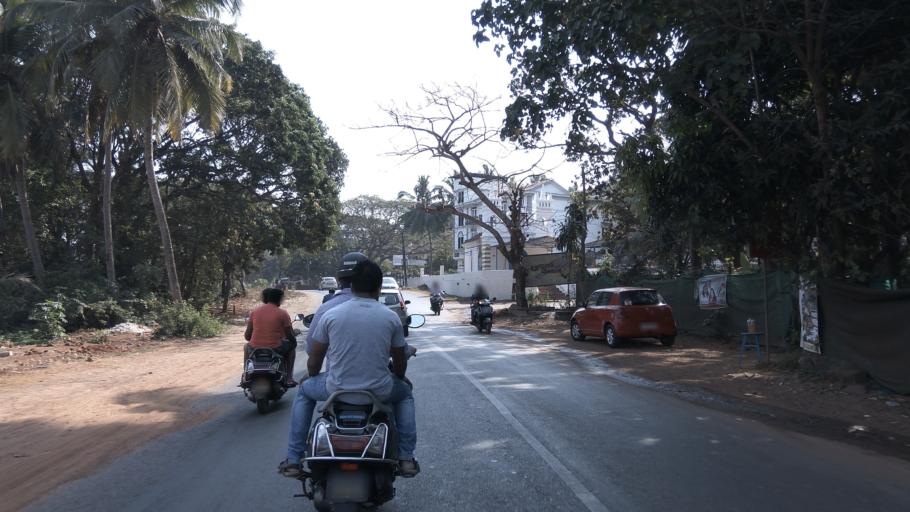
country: IN
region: Goa
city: Calangute
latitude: 15.5416
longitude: 73.7742
